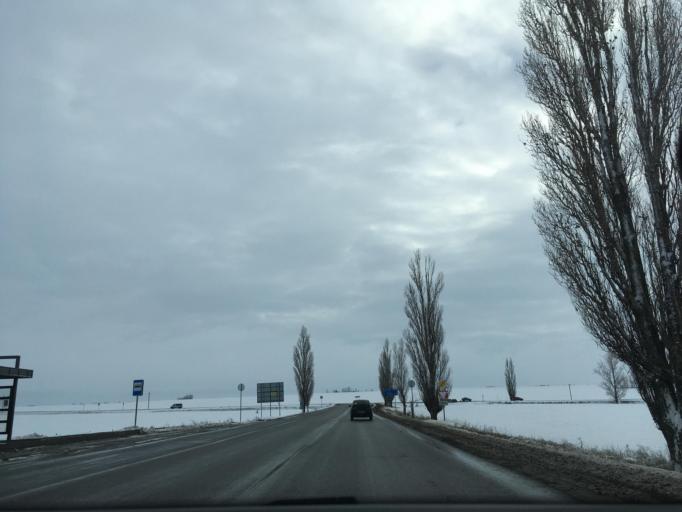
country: UA
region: Luhansk
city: Lozno-Oleksandrivka
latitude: 49.9531
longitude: 38.9535
